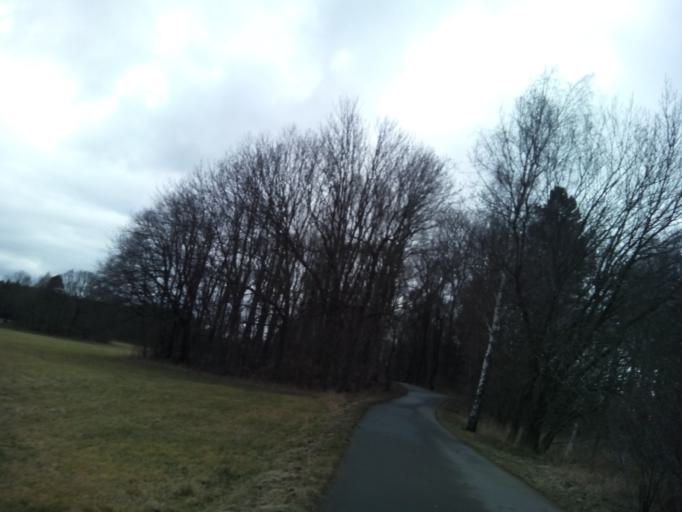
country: DE
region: Saxony
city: Brand-Erbisdorf
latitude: 50.8835
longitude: 13.3312
